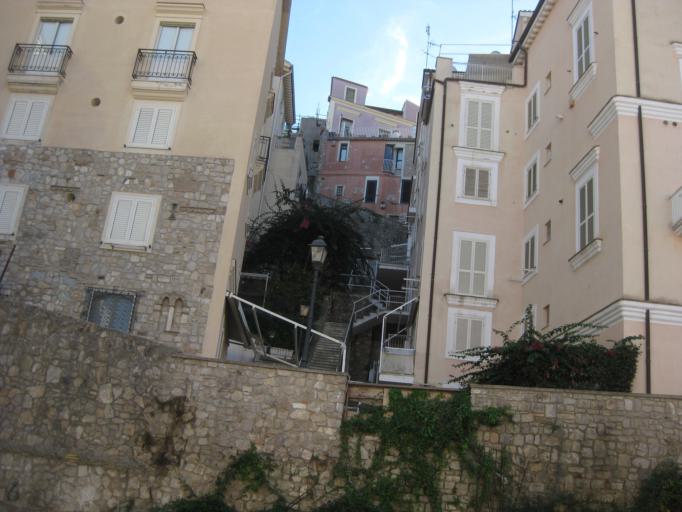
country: IT
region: Latium
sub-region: Provincia di Latina
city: Gaeta
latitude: 41.2083
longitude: 13.5877
